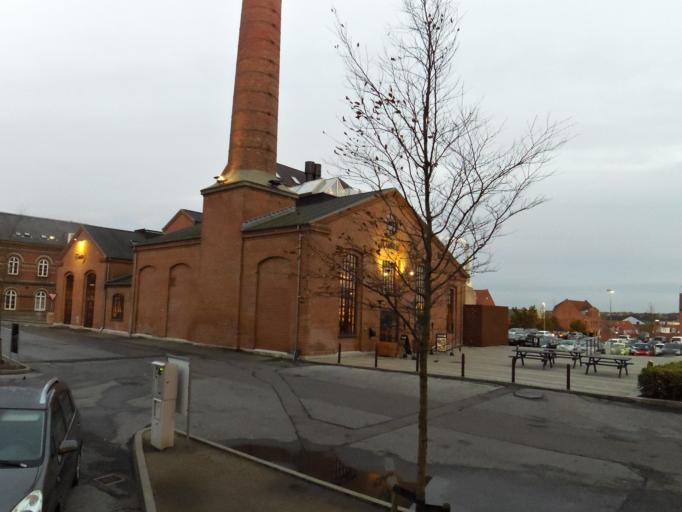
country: DK
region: Central Jutland
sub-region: Randers Kommune
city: Randers
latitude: 56.4635
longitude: 10.0381
